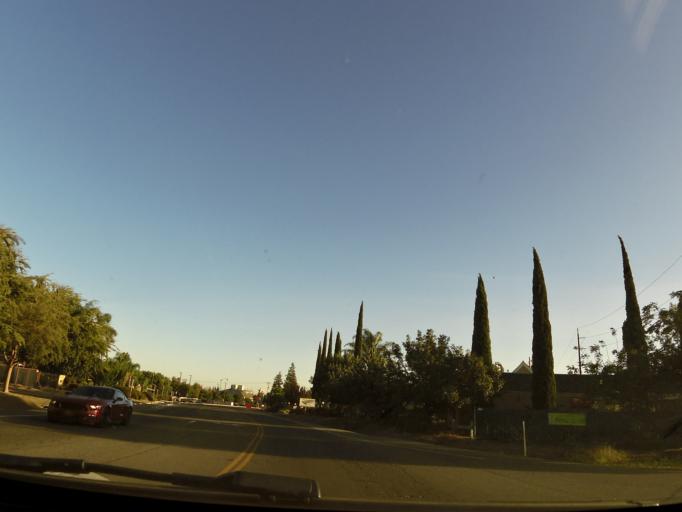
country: US
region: California
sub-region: San Joaquin County
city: Lathrop
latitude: 37.8287
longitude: -121.2880
